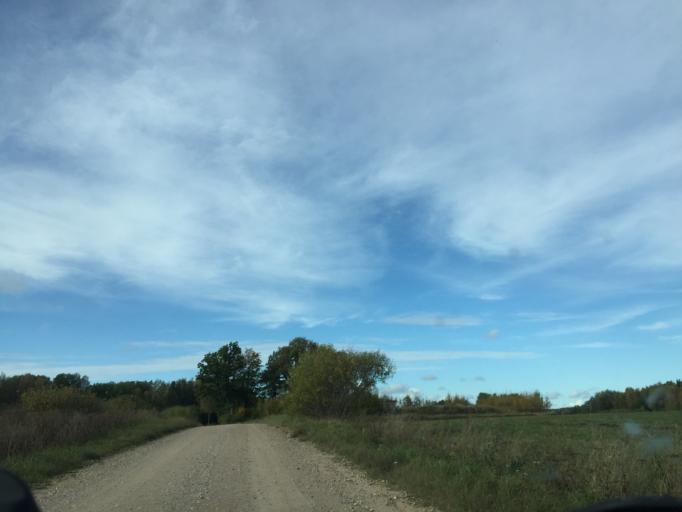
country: LV
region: Jaunpils
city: Jaunpils
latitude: 56.6096
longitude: 23.0495
